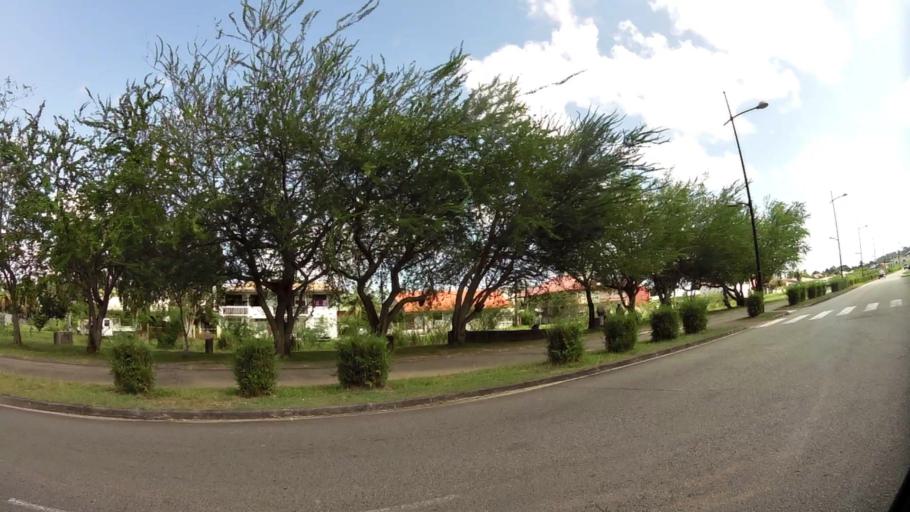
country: GF
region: Guyane
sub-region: Guyane
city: Cayenne
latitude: 4.9216
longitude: -52.3170
